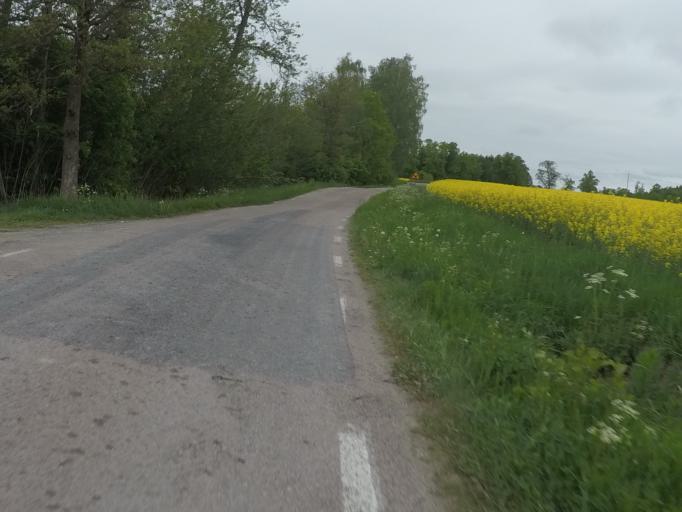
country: SE
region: Vaestmanland
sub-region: Hallstahammars Kommun
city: Kolback
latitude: 59.5519
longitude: 16.2676
